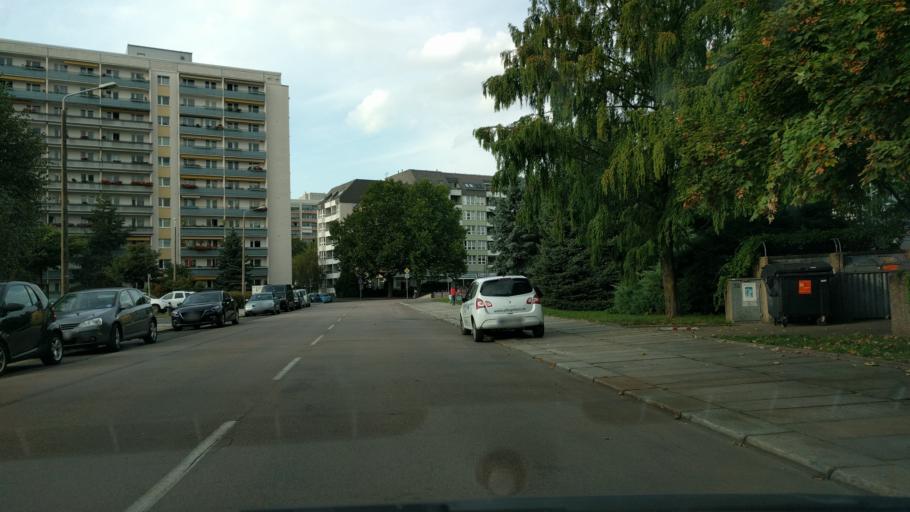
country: DE
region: Saxony
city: Dresden
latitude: 51.0543
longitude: 13.7617
